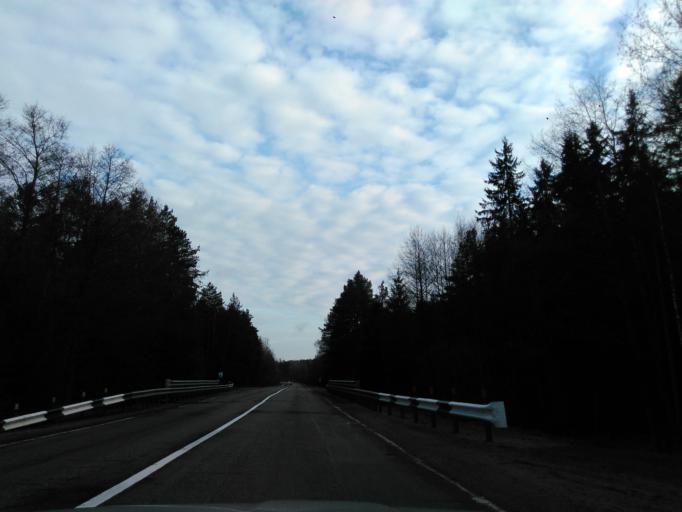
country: BY
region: Minsk
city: Plyeshchanitsy
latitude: 54.3884
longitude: 27.8721
